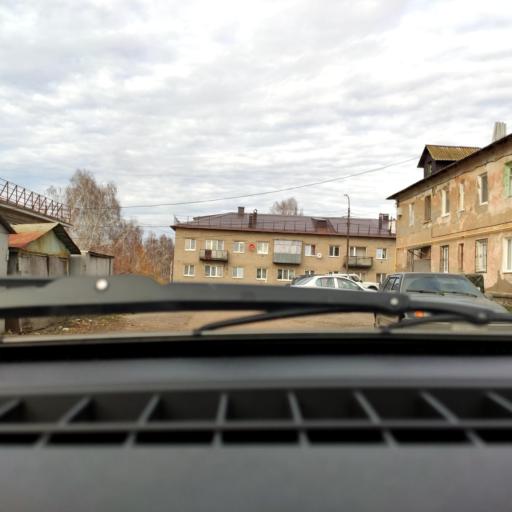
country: RU
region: Bashkortostan
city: Blagoveshchensk
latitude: 54.9008
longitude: 56.1469
